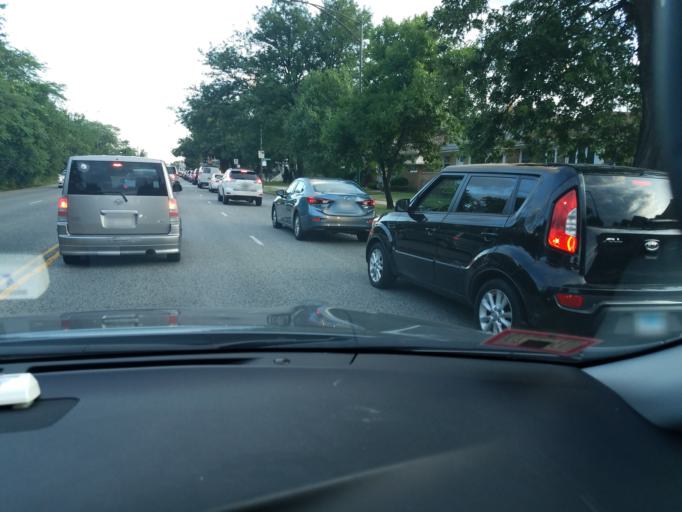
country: US
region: Illinois
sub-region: Cook County
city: Lincolnwood
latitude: 41.9786
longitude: -87.7481
